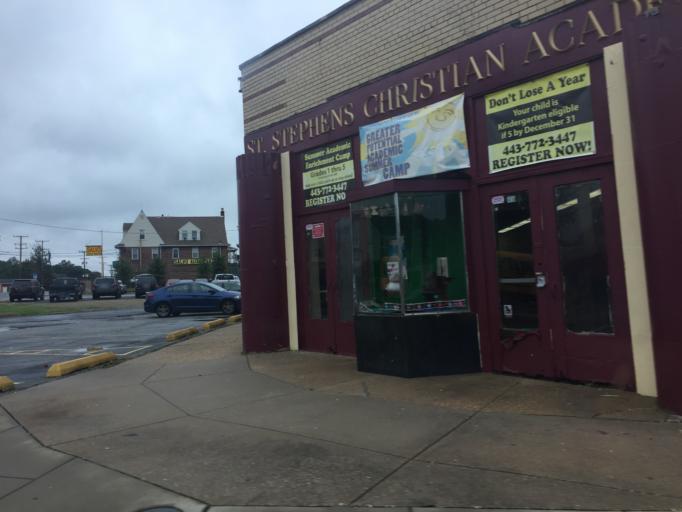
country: US
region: Maryland
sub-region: Baltimore County
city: Middle River
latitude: 39.3150
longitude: -76.4507
